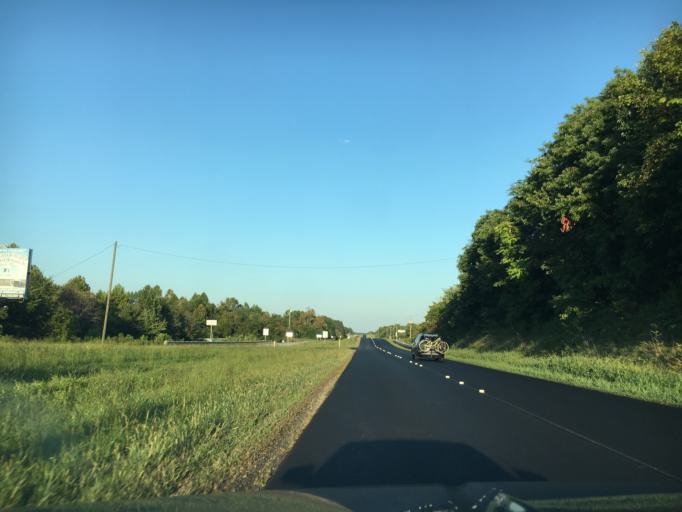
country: US
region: Virginia
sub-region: City of Danville
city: Danville
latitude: 36.5807
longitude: -79.2601
